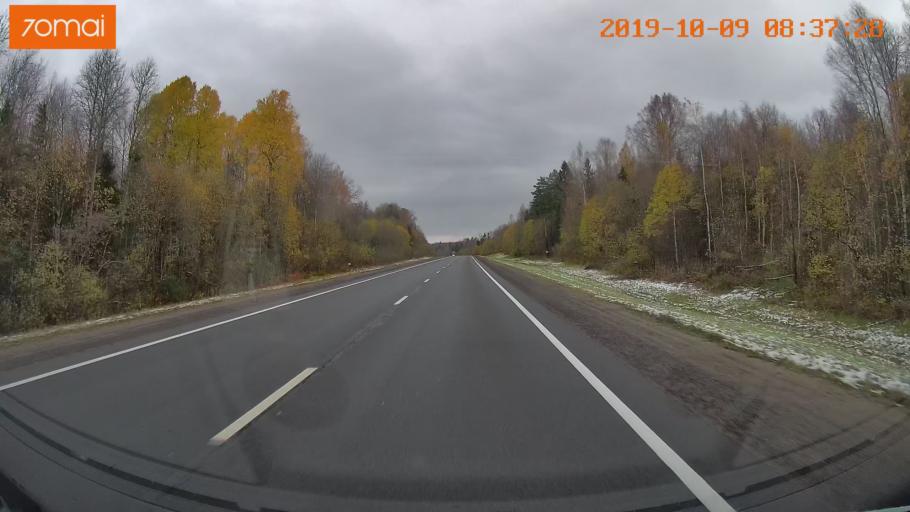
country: RU
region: Vologda
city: Gryazovets
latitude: 58.9419
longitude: 40.1743
